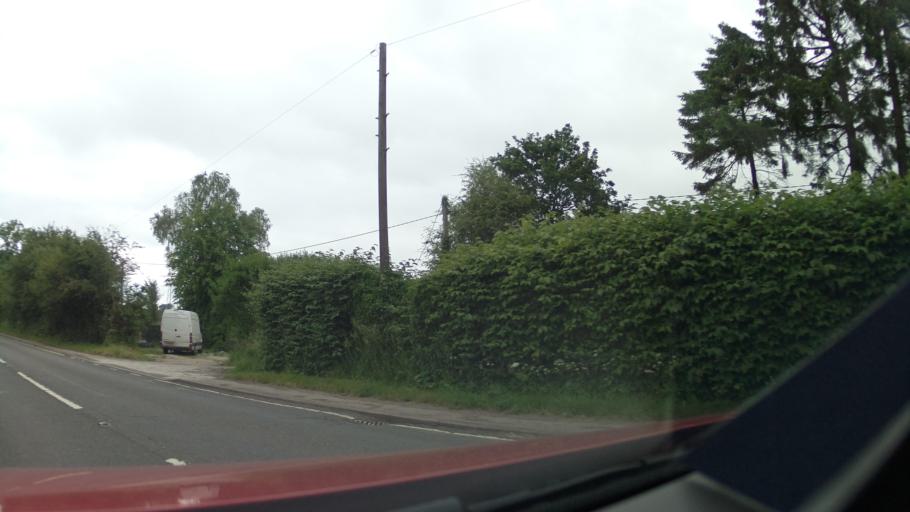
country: GB
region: England
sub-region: Derbyshire
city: Yeldersley
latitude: 52.9605
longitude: -1.5979
